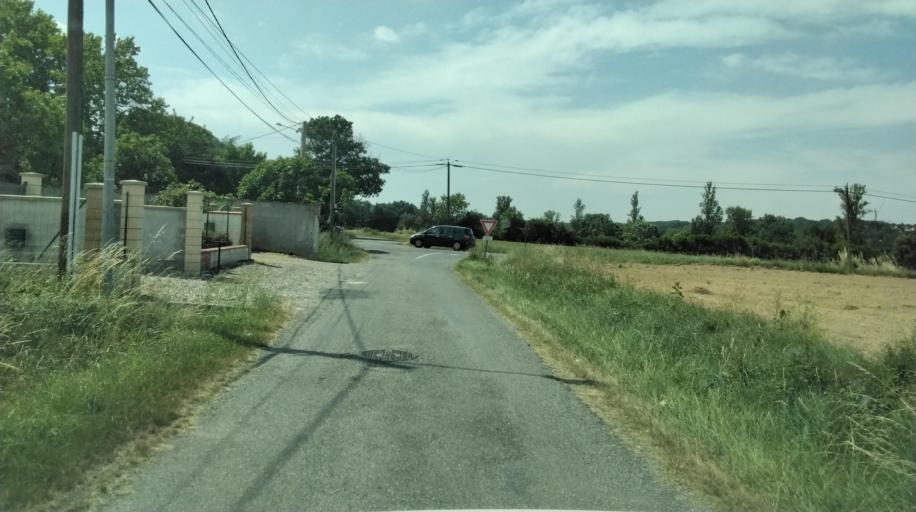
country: FR
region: Midi-Pyrenees
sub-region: Departement de la Haute-Garonne
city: Rieumes
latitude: 43.4161
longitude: 1.1323
